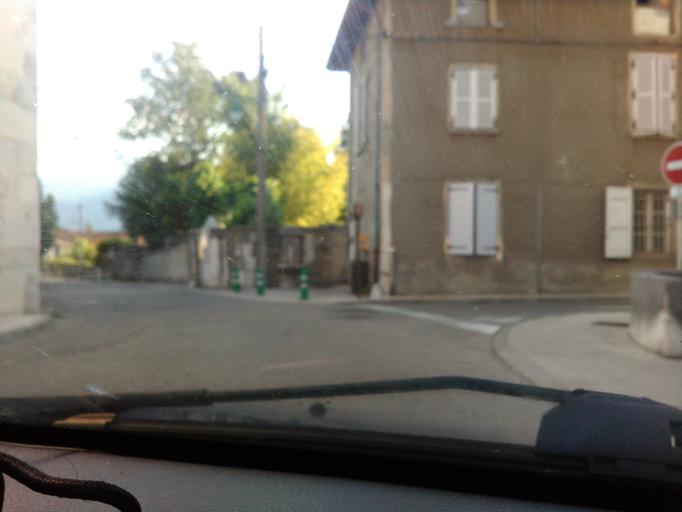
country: FR
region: Rhone-Alpes
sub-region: Departement de l'Isere
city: Saint-Egreve
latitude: 45.2395
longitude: 5.6902
